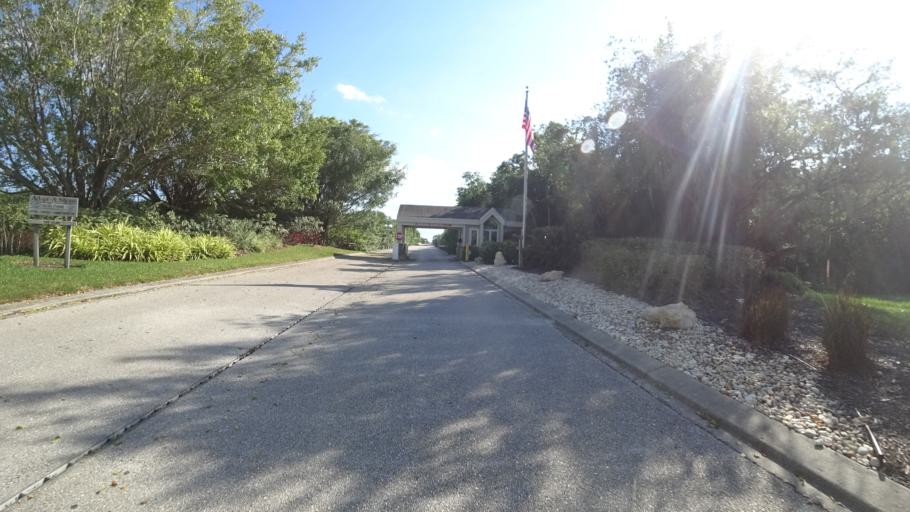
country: US
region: Florida
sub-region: Manatee County
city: Longboat Key
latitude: 27.4500
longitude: -82.6486
